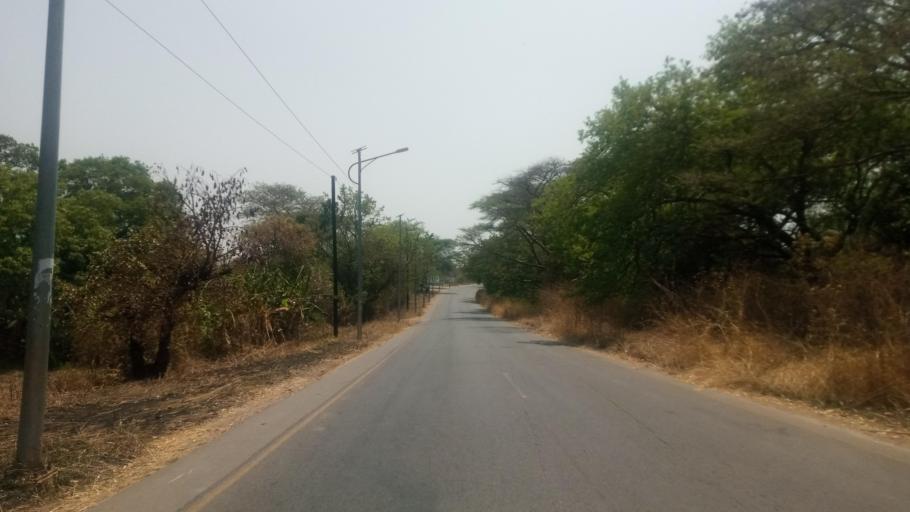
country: ZM
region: Lusaka
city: Lusaka
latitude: -15.4605
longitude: 28.4351
